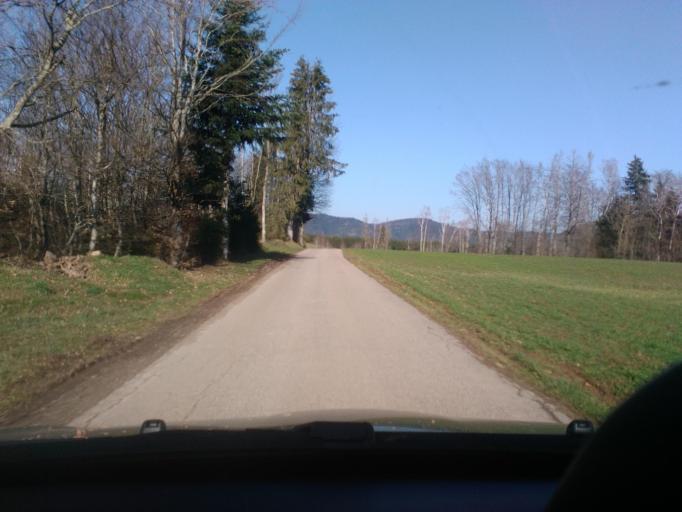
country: FR
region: Lorraine
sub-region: Departement des Vosges
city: Moyenmoutier
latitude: 48.3645
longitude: 6.9171
